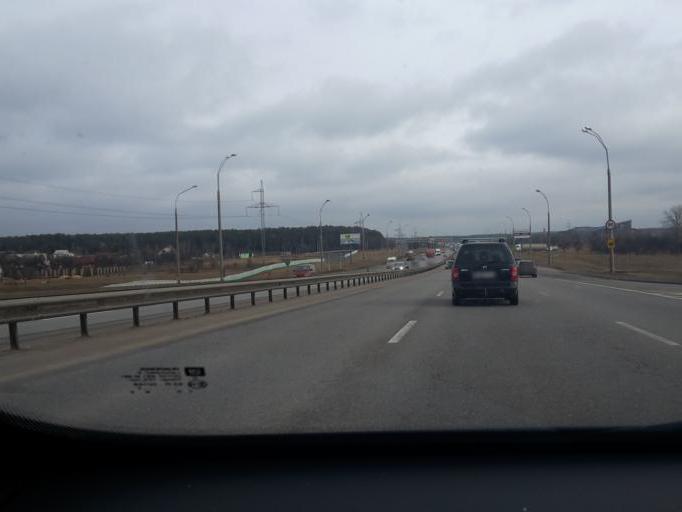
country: BY
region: Minsk
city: Zhdanovichy
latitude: 53.9452
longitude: 27.4382
